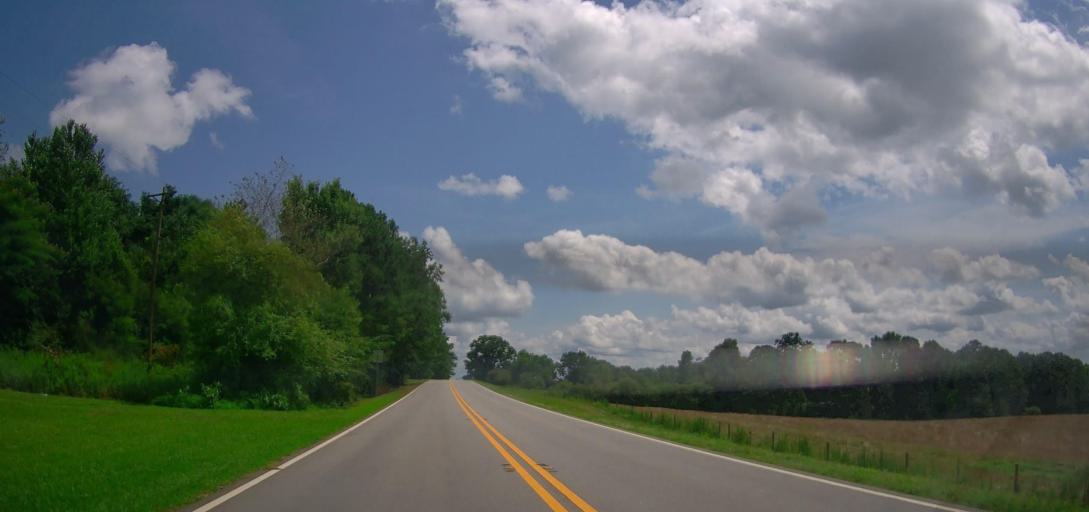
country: US
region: Georgia
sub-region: Carroll County
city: Bowdon
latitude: 33.4303
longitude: -85.2691
